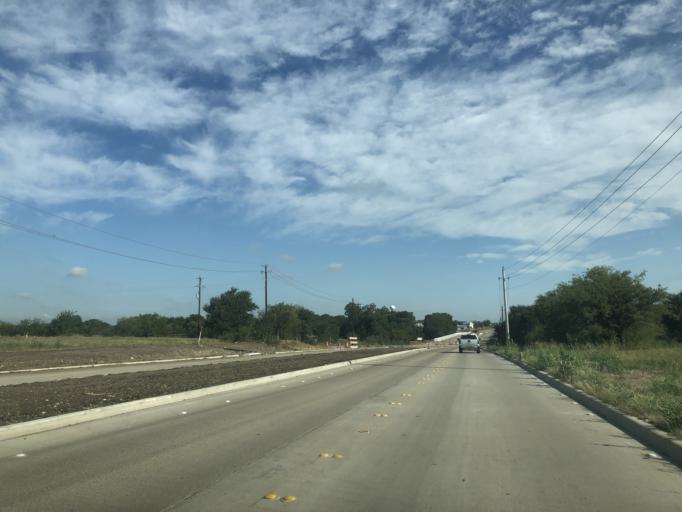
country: US
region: Texas
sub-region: Denton County
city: Justin
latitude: 33.0734
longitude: -97.2955
